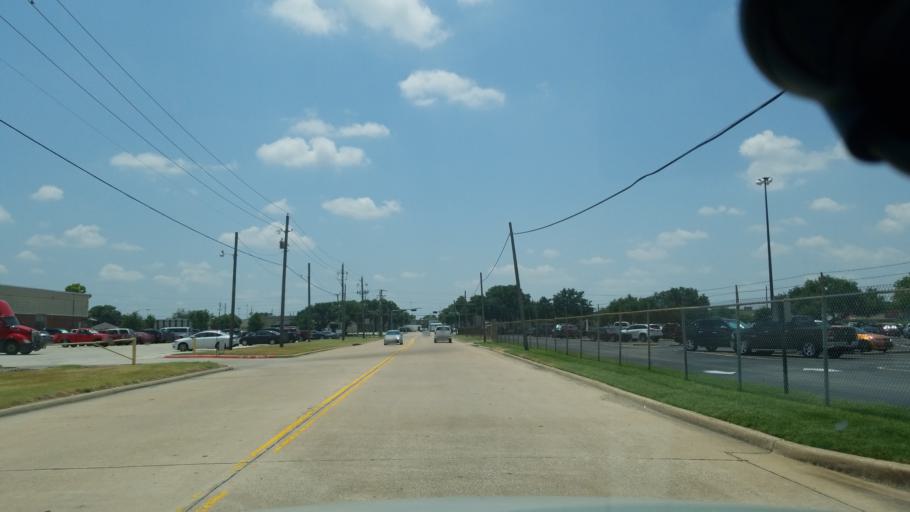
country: US
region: Texas
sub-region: Dallas County
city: Carrollton
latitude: 32.9551
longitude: -96.8686
